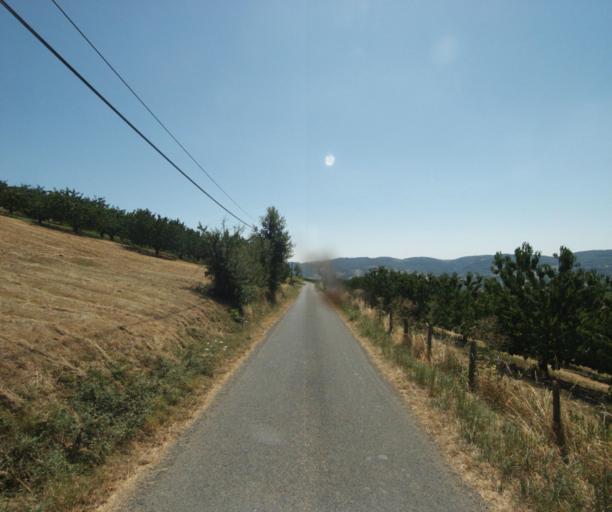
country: FR
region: Rhone-Alpes
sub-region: Departement du Rhone
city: Bessenay
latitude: 45.7842
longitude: 4.5300
